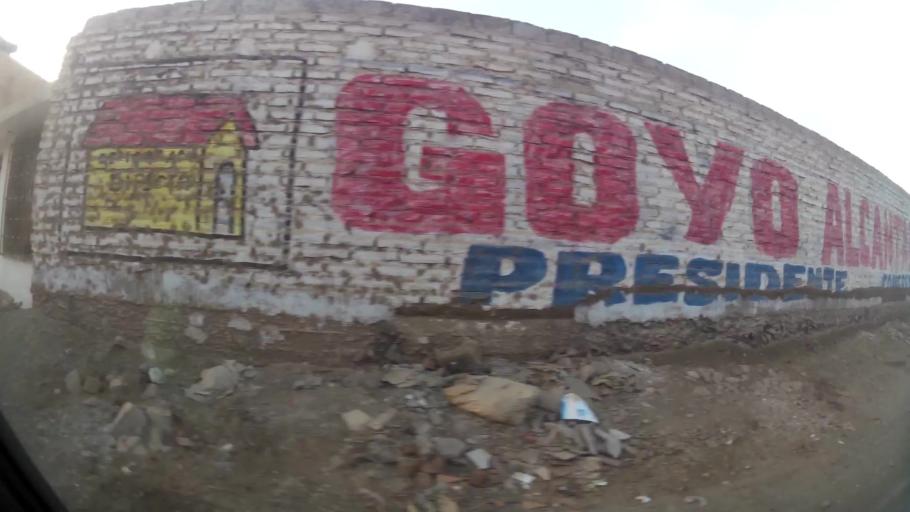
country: PE
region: Lima
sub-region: Huaura
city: Huacho
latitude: -11.1186
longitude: -77.6078
